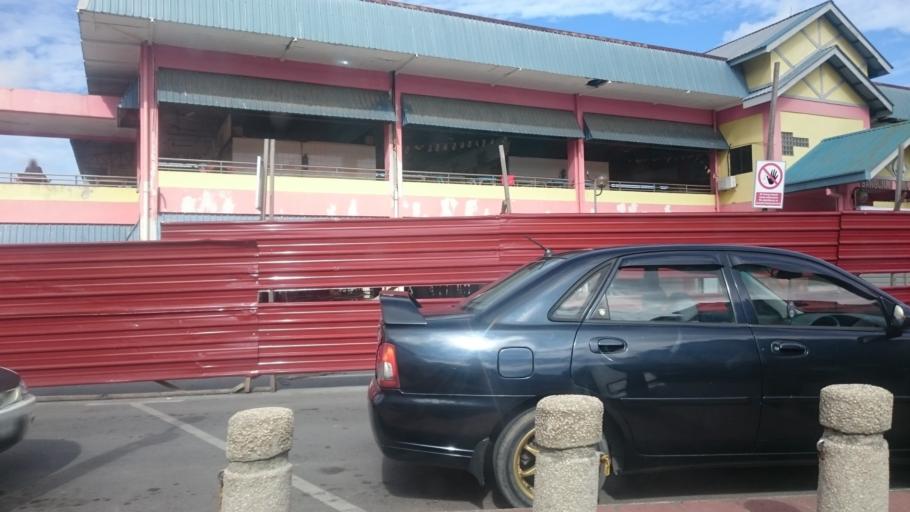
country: MY
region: Sarawak
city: Limbang
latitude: 4.7541
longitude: 115.0090
